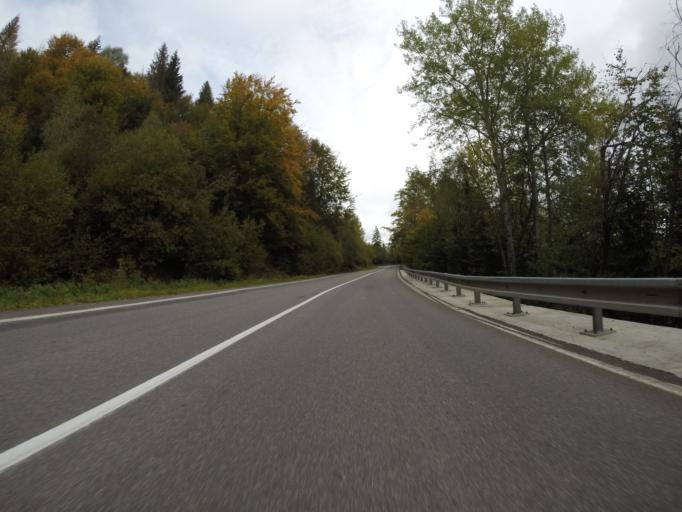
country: SK
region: Banskobystricky
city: Cierny Balog
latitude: 48.5945
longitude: 19.7263
